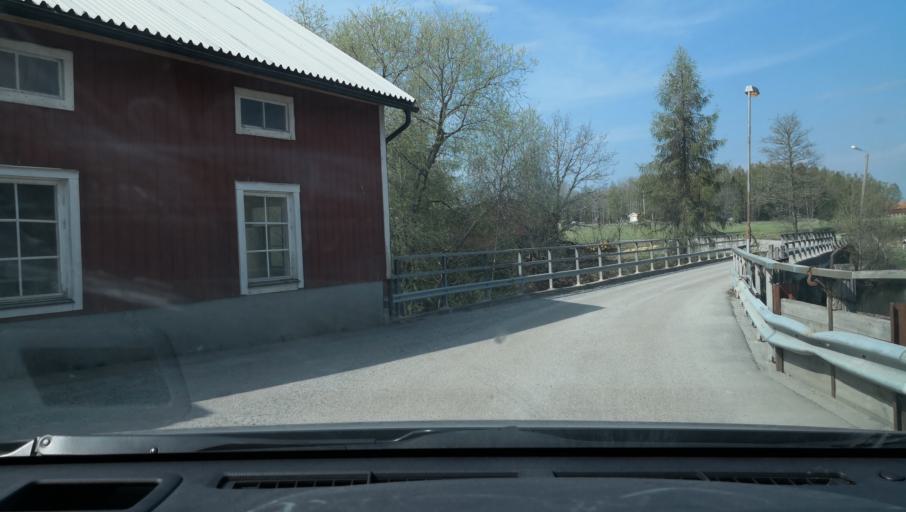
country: SE
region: Vaestmanland
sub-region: Vasteras
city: Skultuna
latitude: 59.7688
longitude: 16.4471
